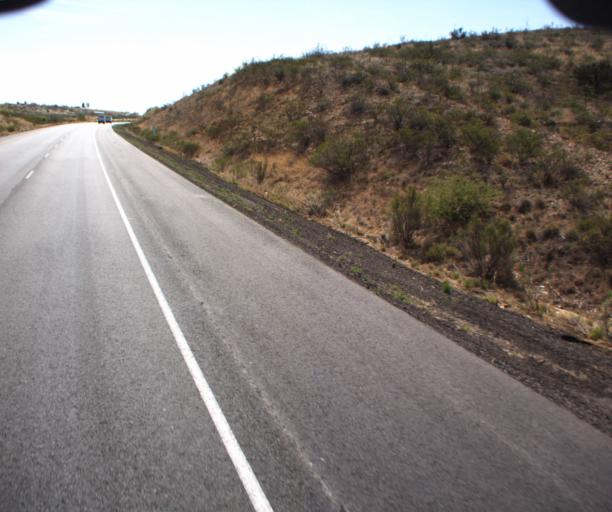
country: US
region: Arizona
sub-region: Cochise County
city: Mescal
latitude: 31.9684
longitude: -110.4716
